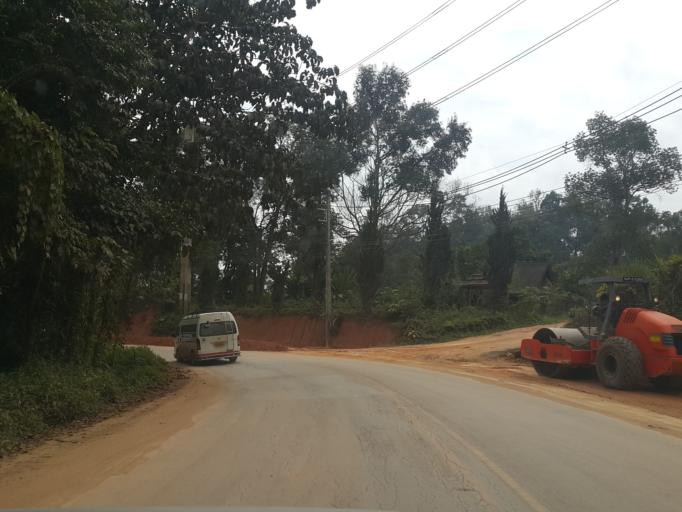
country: TH
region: Chiang Mai
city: Mae Taeng
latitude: 19.1261
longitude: 98.7071
